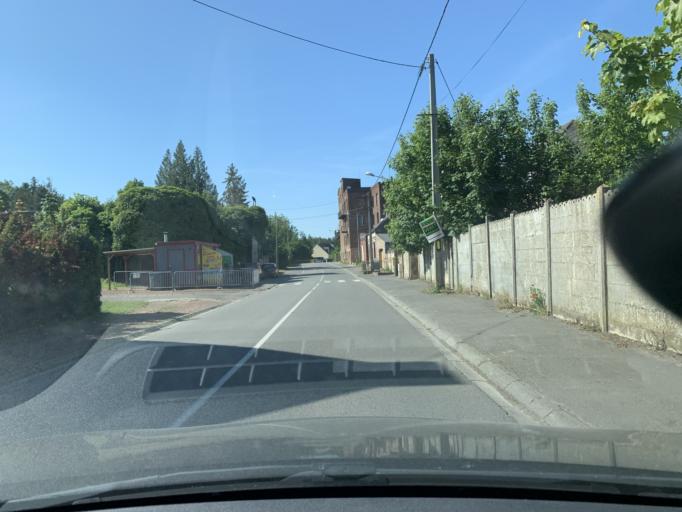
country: FR
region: Nord-Pas-de-Calais
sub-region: Departement du Nord
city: Rumilly-en-Cambresis
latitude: 50.1059
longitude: 3.2484
